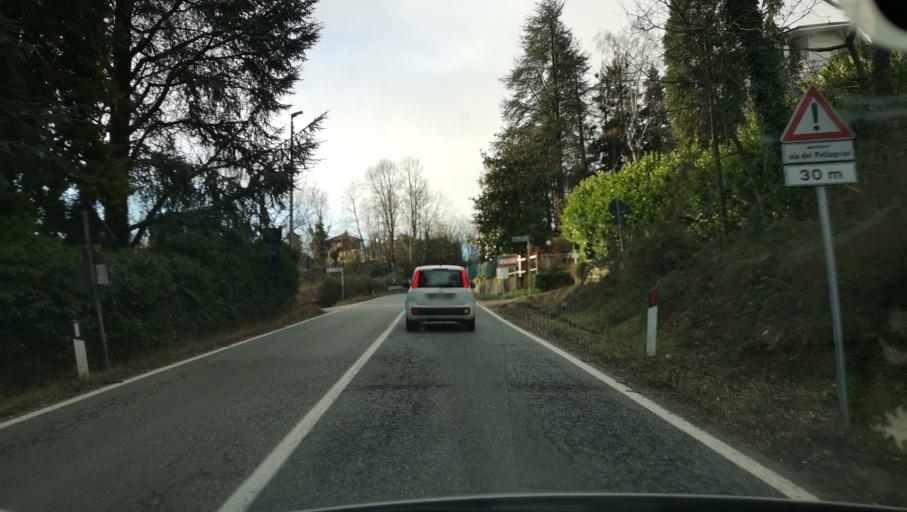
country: IT
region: Piedmont
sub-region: Provincia di Torino
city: Giaveno
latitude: 45.0500
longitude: 7.3744
